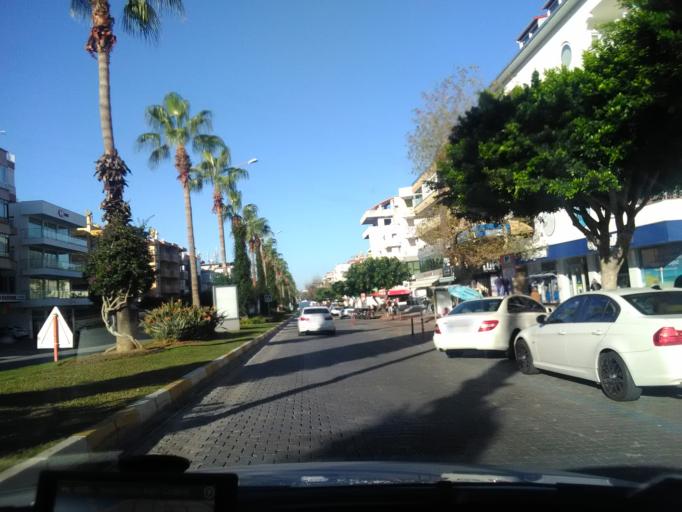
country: TR
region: Antalya
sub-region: Alanya
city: Alanya
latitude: 36.5450
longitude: 31.9939
